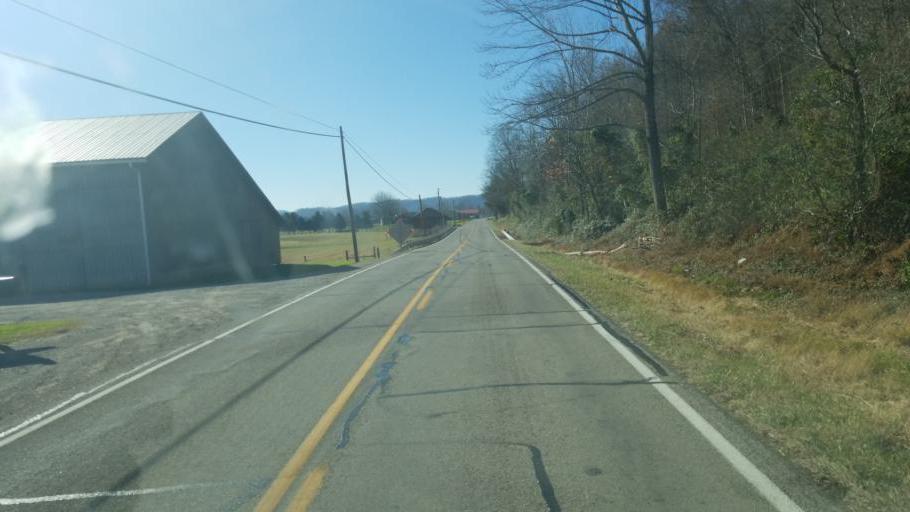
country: US
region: Kentucky
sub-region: Lewis County
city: Vanceburg
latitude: 38.6322
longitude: -83.1520
